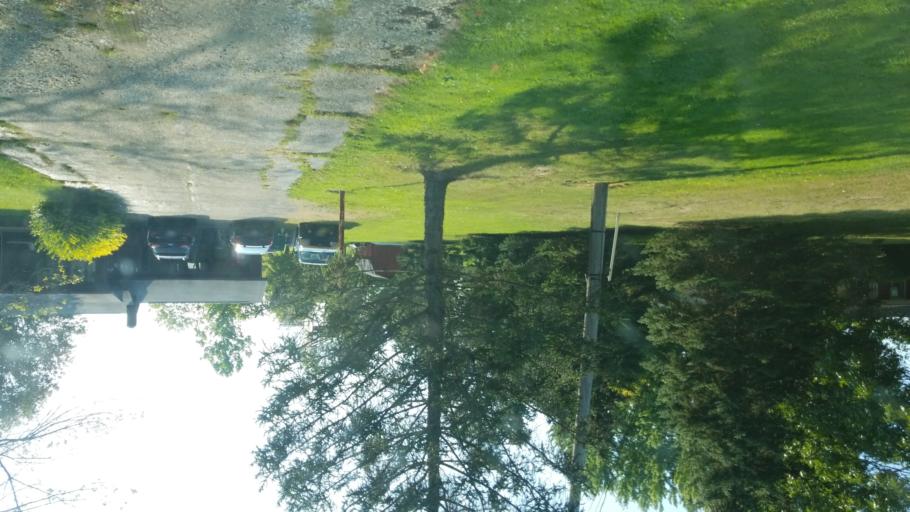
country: US
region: Ohio
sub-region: Geauga County
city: Middlefield
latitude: 41.4045
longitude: -81.0601
